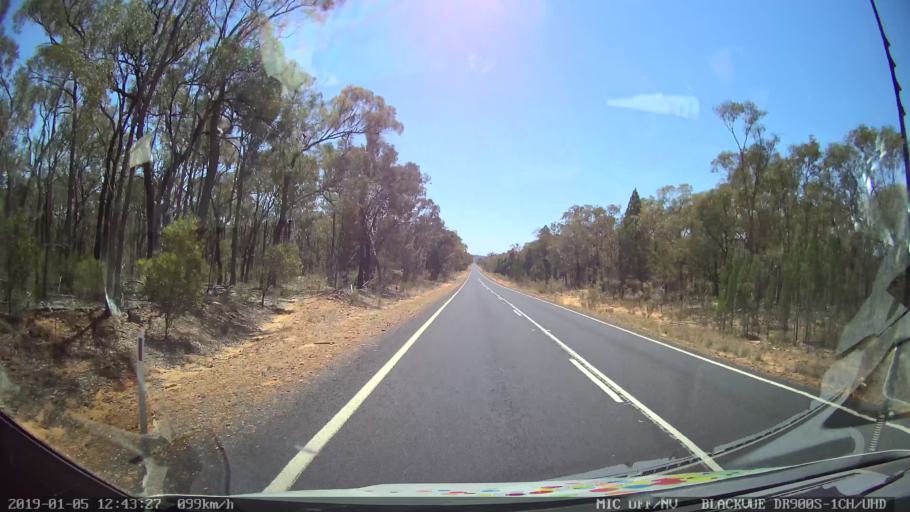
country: AU
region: New South Wales
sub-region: Warrumbungle Shire
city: Coonabarabran
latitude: -31.1480
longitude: 149.5242
